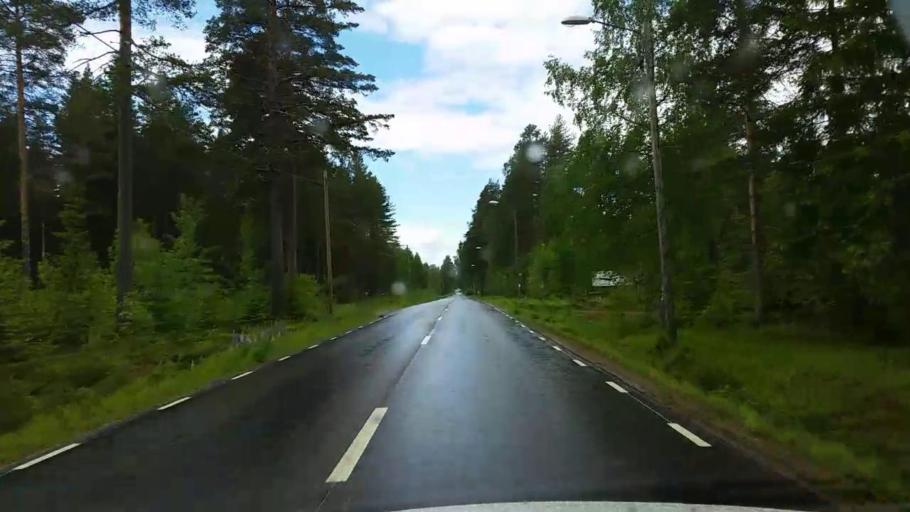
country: SE
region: Gaevleborg
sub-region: Sandvikens Kommun
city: Jarbo
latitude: 60.8385
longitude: 16.4850
